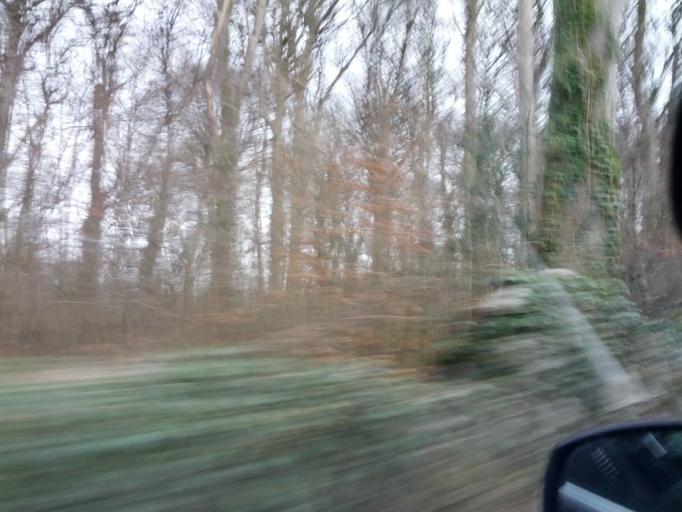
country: IE
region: Connaught
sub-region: County Galway
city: Oranmore
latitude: 53.1789
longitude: -8.9002
